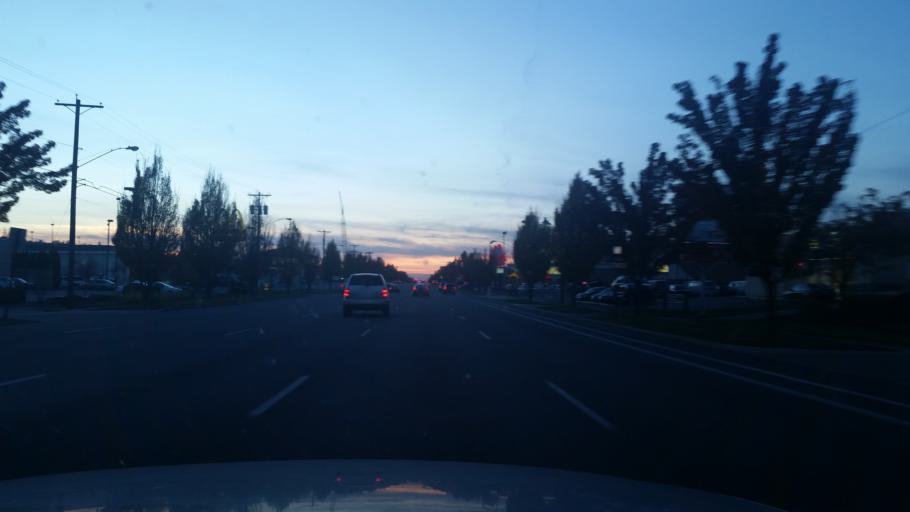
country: US
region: Washington
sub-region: Spokane County
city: Dishman
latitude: 47.6571
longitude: -117.2628
